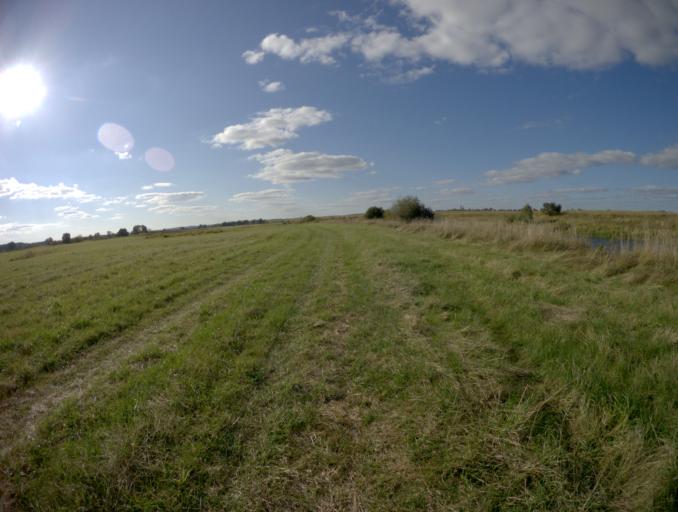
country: RU
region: Vladimir
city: Orgtrud
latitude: 56.3096
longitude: 40.6602
